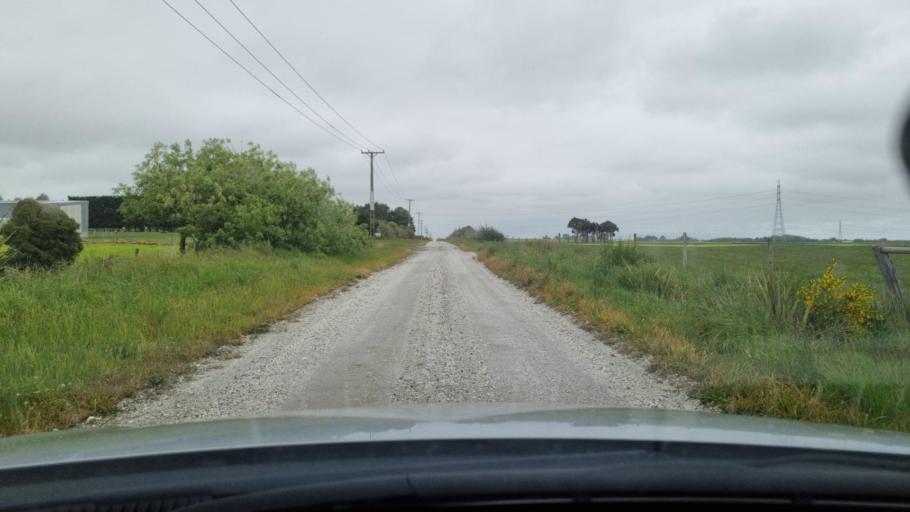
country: NZ
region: Southland
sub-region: Invercargill City
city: Invercargill
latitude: -46.4426
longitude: 168.4352
